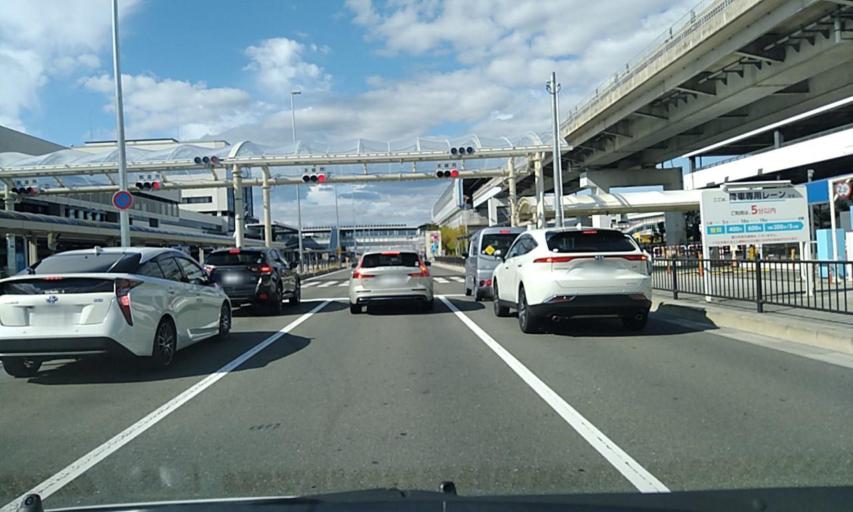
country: JP
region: Osaka
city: Toyonaka
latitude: 34.7901
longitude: 135.4433
